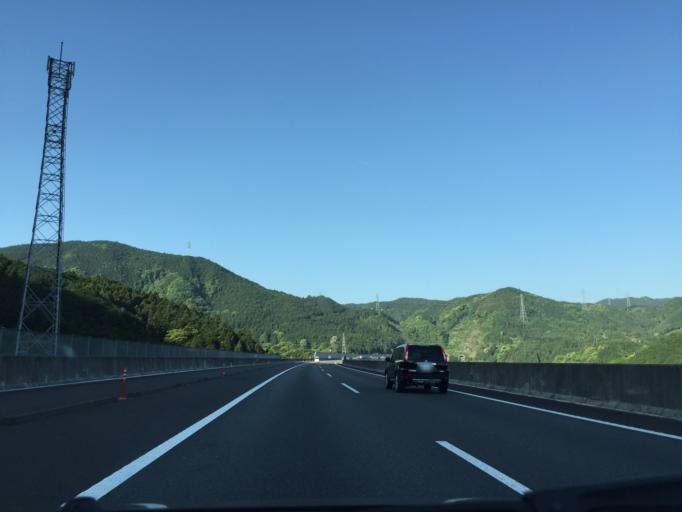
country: JP
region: Shizuoka
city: Fujinomiya
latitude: 35.1729
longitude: 138.6031
